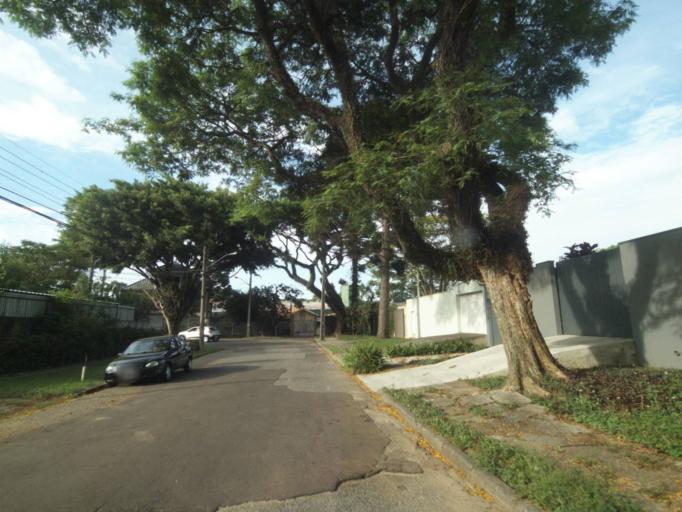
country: BR
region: Parana
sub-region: Curitiba
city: Curitiba
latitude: -25.4297
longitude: -49.2322
